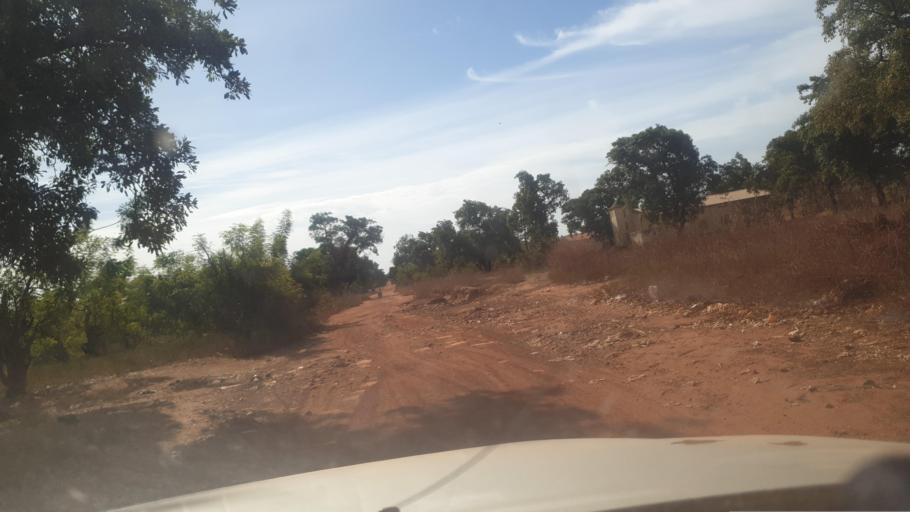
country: ML
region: Sikasso
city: Sikasso
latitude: 11.8396
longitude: -6.0104
